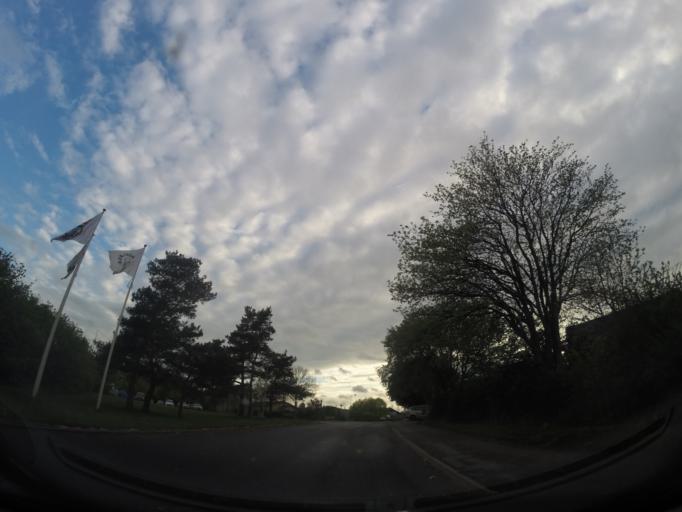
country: DK
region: Capital Region
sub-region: Hoje-Taastrup Kommune
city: Taastrup
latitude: 55.6811
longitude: 12.2425
